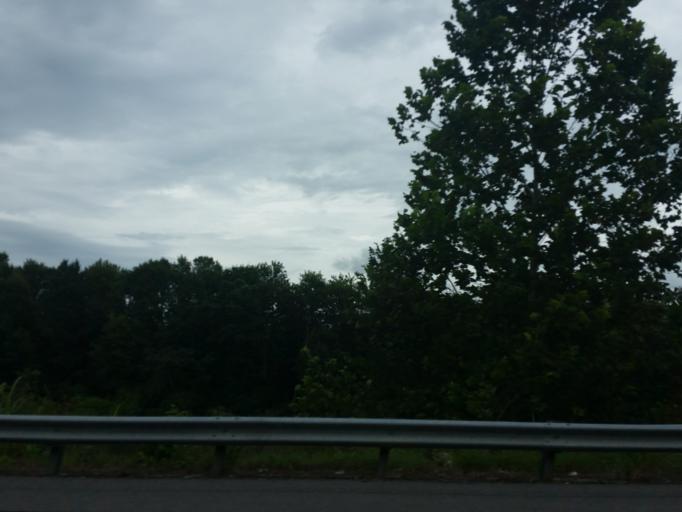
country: US
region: Kentucky
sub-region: Ballard County
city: Wickliffe
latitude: 36.9842
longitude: -89.1064
